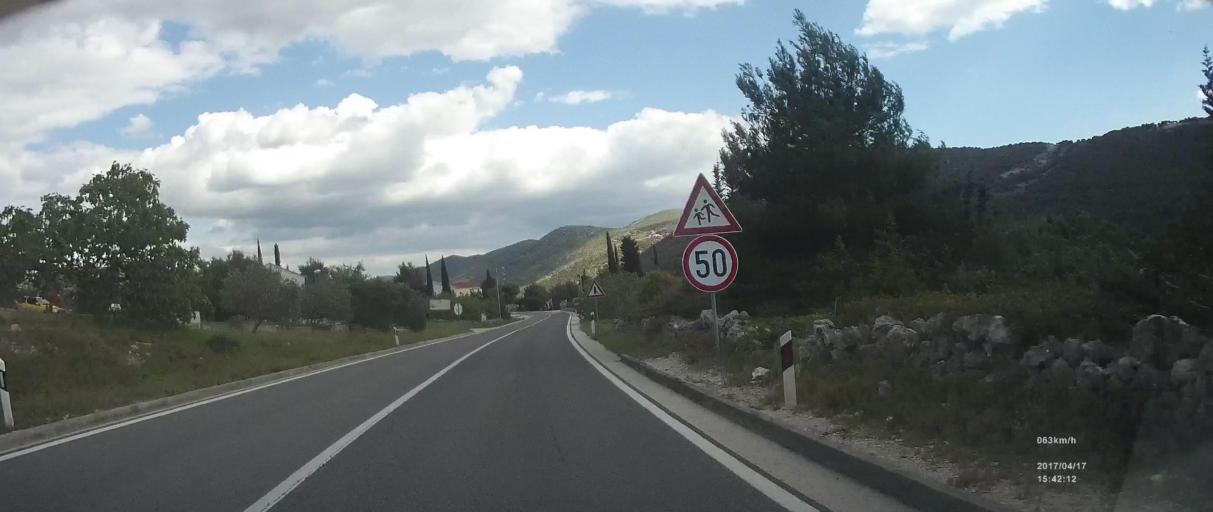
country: HR
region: Sibensko-Kniniska
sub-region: Grad Sibenik
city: Brodarica
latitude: 43.6378
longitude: 15.9639
